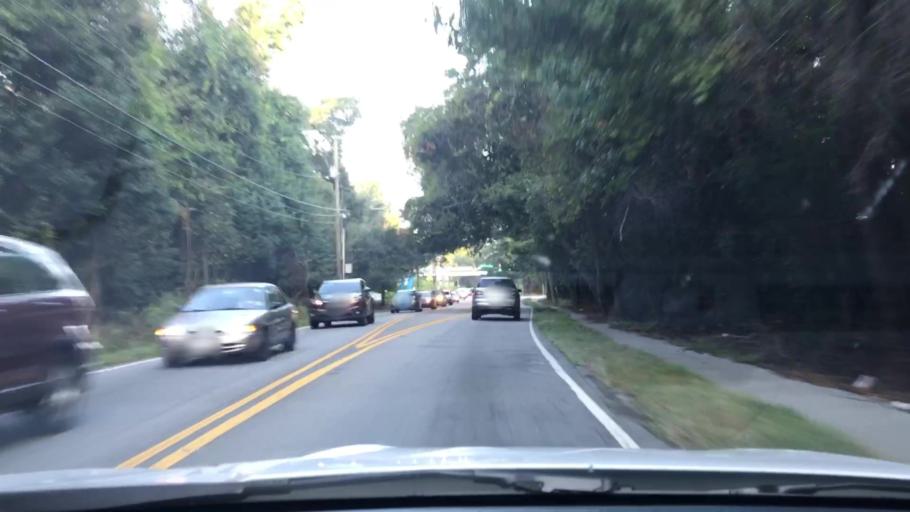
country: US
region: South Carolina
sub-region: Charleston County
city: North Charleston
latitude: 32.8142
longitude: -80.0310
